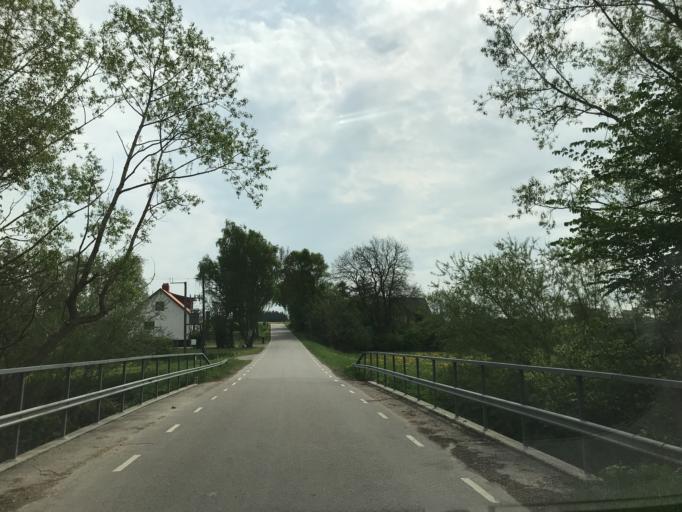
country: SE
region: Skane
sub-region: Svalovs Kommun
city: Teckomatorp
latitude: 55.8467
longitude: 13.0723
